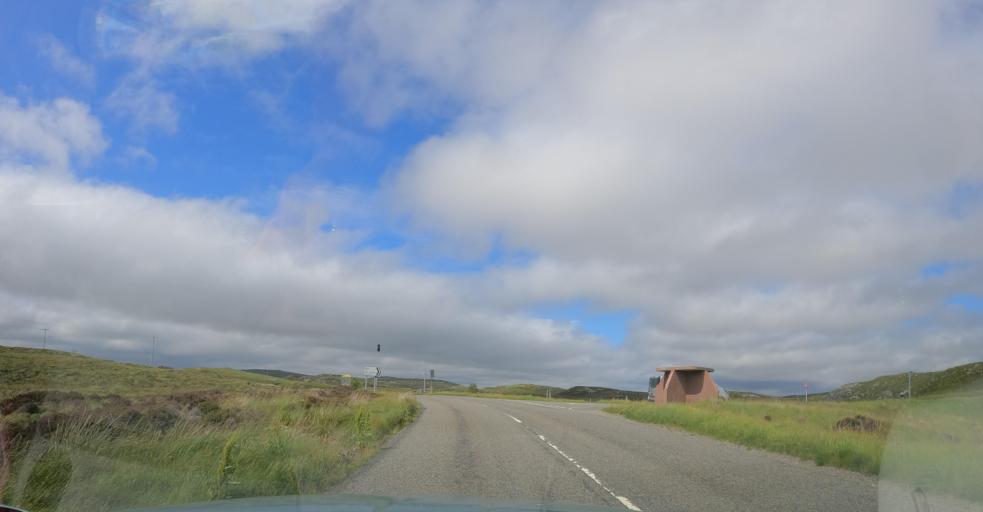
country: GB
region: Scotland
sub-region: Eilean Siar
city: Stornoway
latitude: 58.1111
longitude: -6.5096
